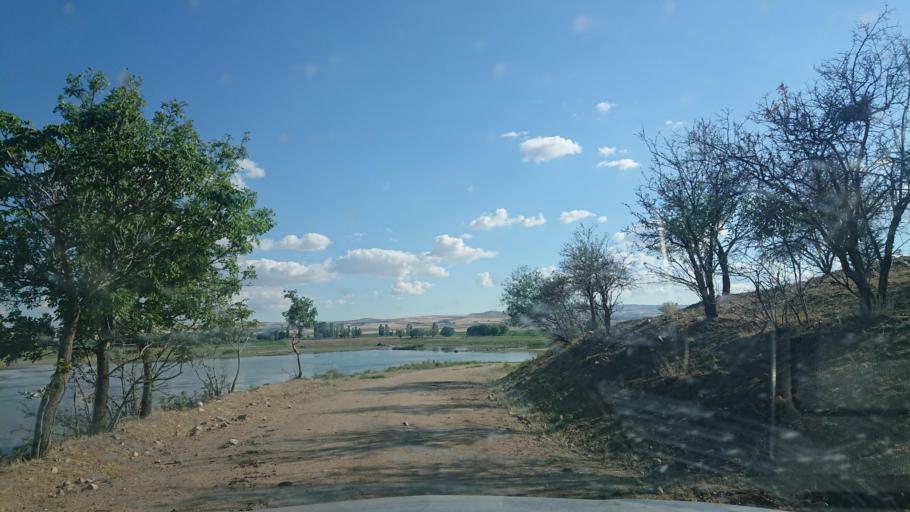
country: TR
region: Aksaray
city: Sariyahsi
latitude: 39.0198
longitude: 33.8962
